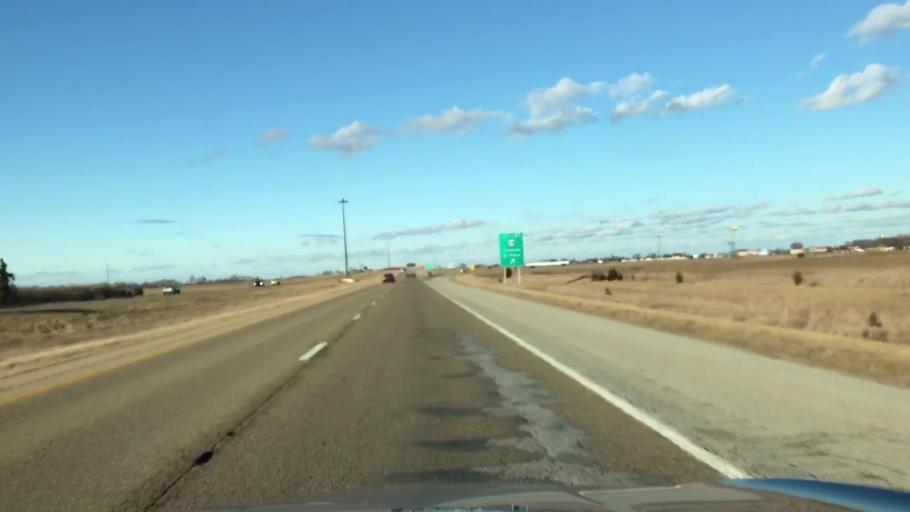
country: US
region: Illinois
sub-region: McLean County
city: Chenoa
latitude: 40.7340
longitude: -88.7374
